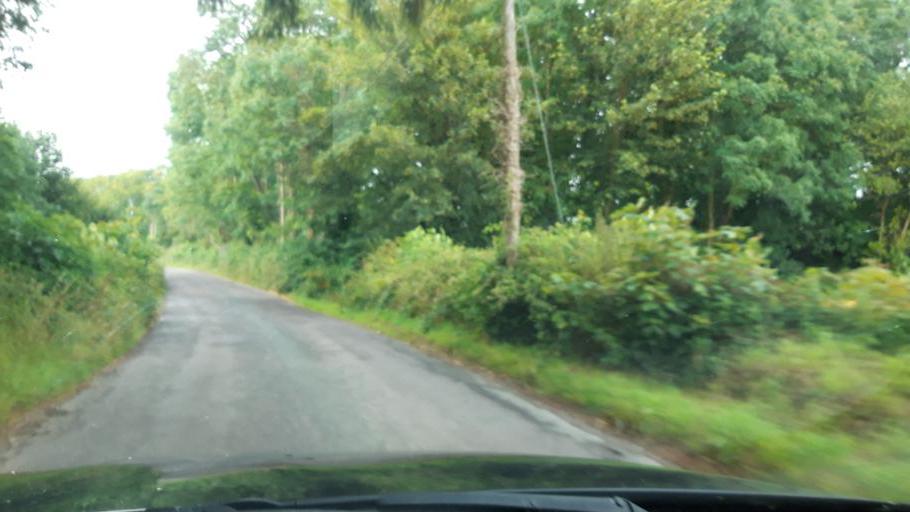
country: IE
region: Munster
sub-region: County Cork
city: Youghal
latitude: 52.1270
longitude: -7.9720
